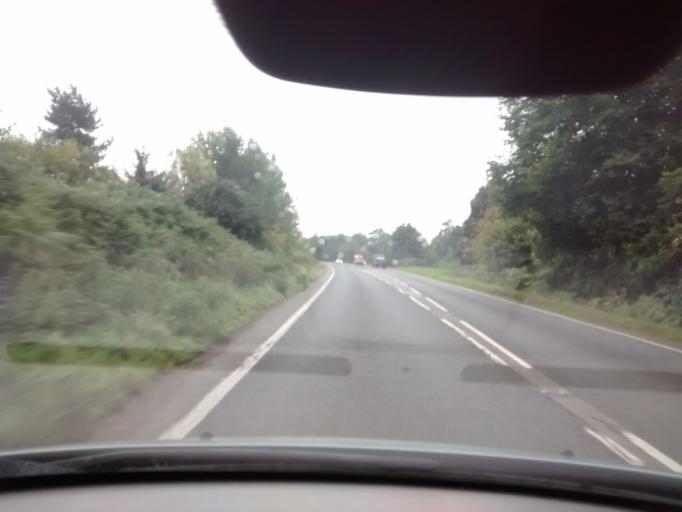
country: GB
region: England
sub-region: Hampshire
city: Ringwood
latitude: 50.8707
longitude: -1.7917
